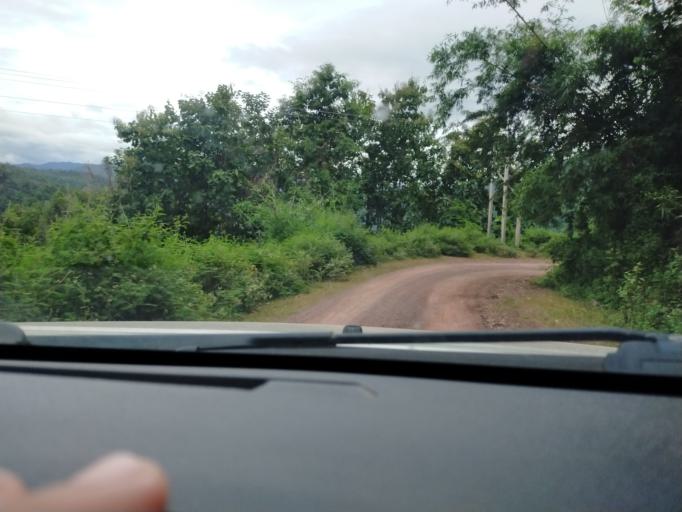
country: TH
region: Nan
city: Chaloem Phra Kiat
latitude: 19.7743
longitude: 101.3517
